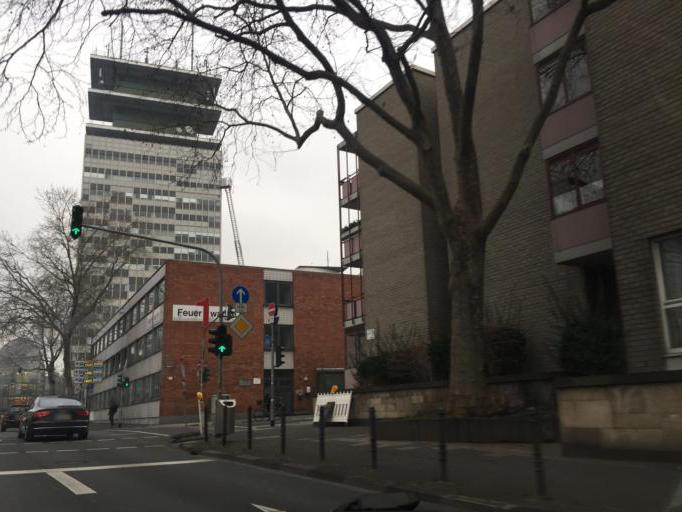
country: DE
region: North Rhine-Westphalia
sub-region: Regierungsbezirk Koln
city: Koeln
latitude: 50.9331
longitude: 6.9536
